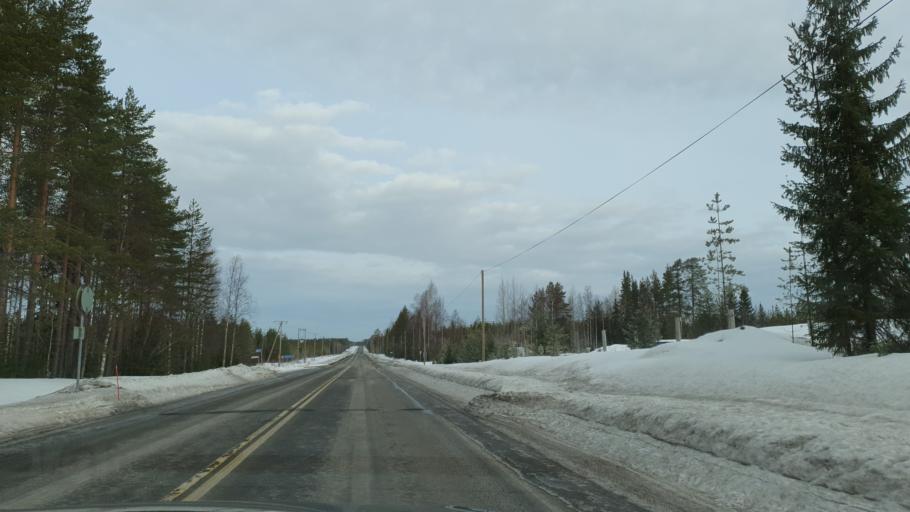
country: FI
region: Kainuu
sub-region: Kajaani
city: Vuokatti
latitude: 64.2032
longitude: 28.1572
